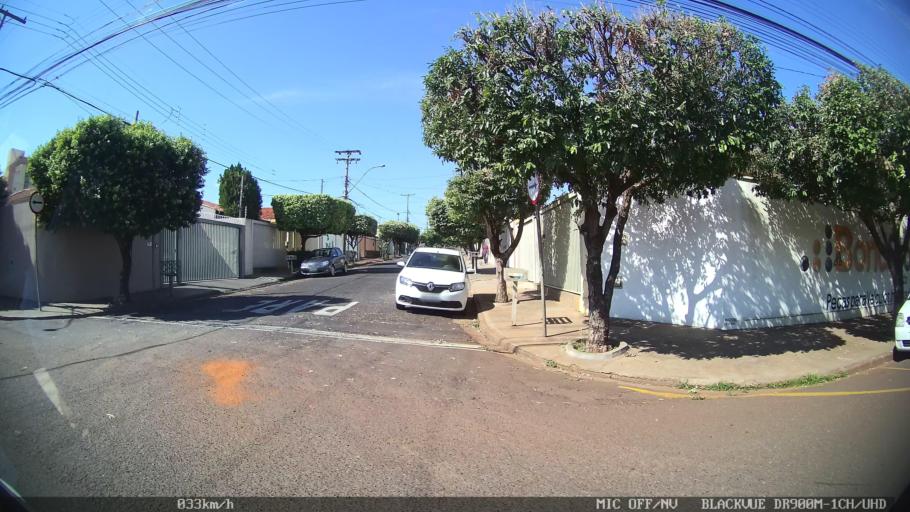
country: BR
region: Sao Paulo
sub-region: Sao Jose Do Rio Preto
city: Sao Jose do Rio Preto
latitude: -20.8034
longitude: -49.3993
